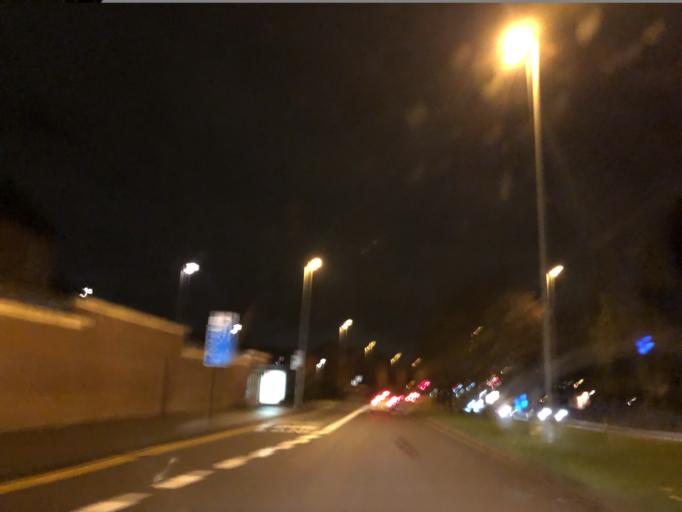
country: GB
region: England
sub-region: Borough of Oldham
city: Oldham
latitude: 53.5325
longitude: -2.1146
